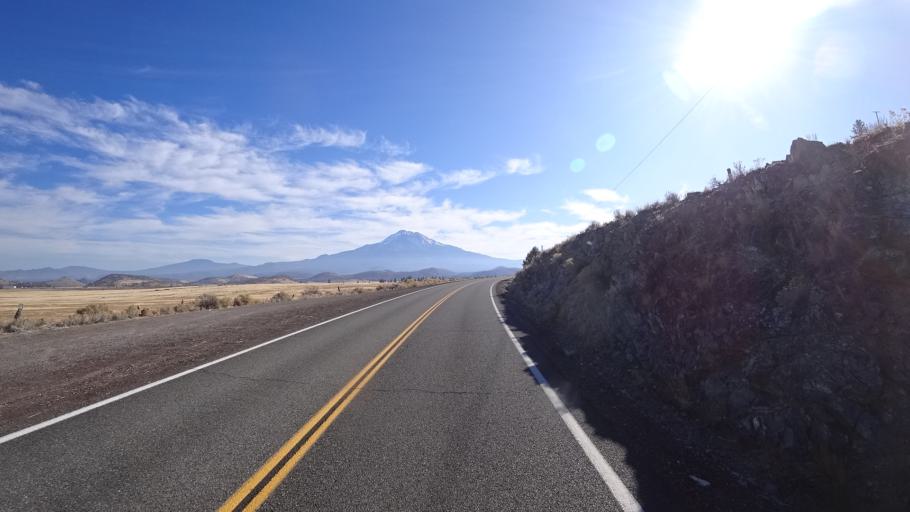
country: US
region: California
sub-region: Siskiyou County
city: Weed
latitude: 41.4680
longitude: -122.4688
